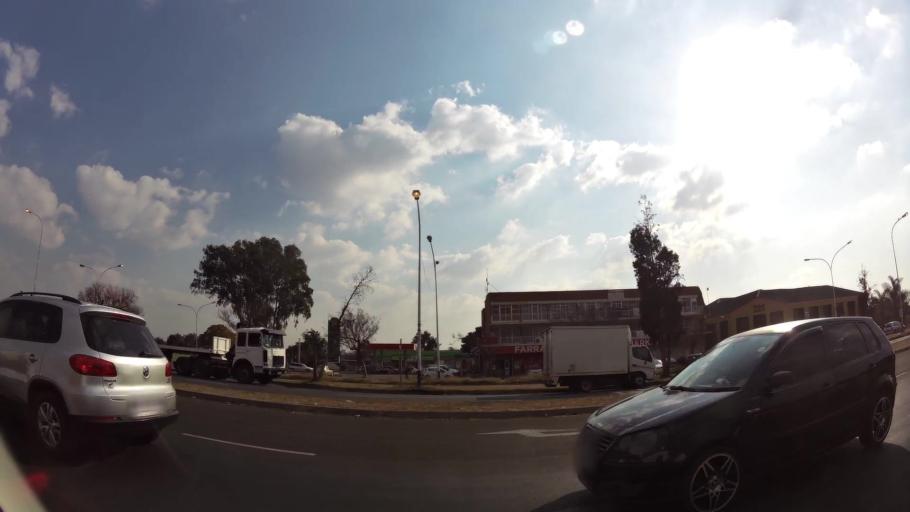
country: ZA
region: Gauteng
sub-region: Ekurhuleni Metropolitan Municipality
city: Boksburg
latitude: -26.2462
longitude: 28.2460
